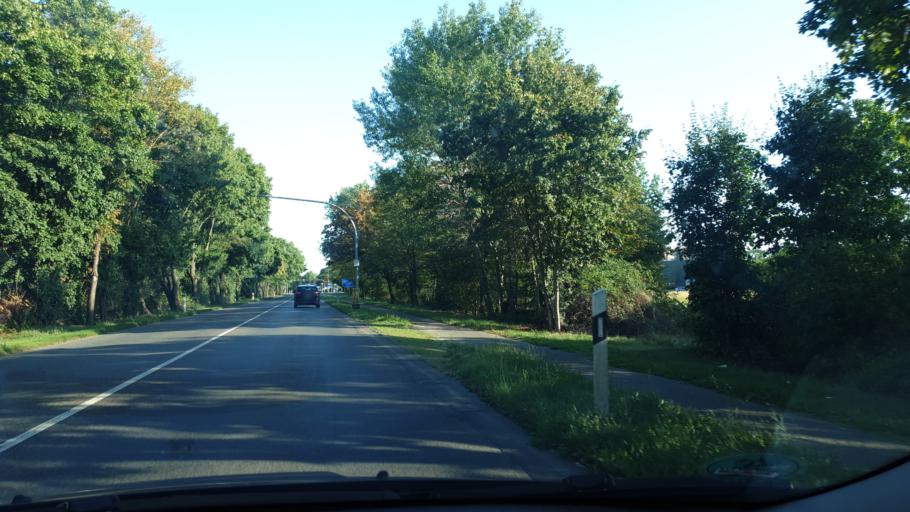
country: DE
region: North Rhine-Westphalia
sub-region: Regierungsbezirk Koln
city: Gremberghoven
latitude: 50.9110
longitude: 7.0569
